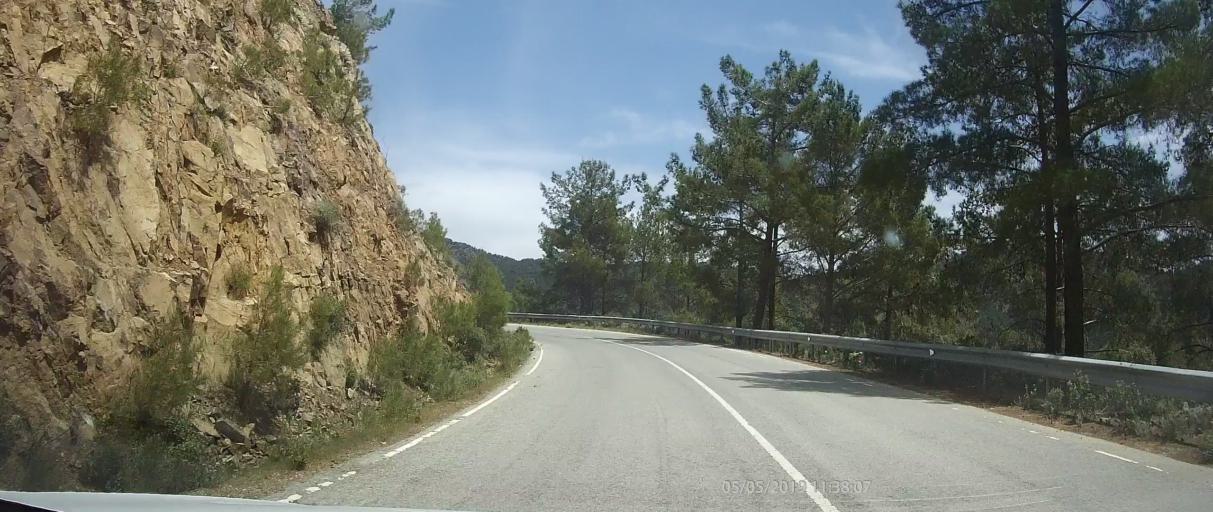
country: CY
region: Lefkosia
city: Kato Pyrgos
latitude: 34.9769
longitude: 32.6607
